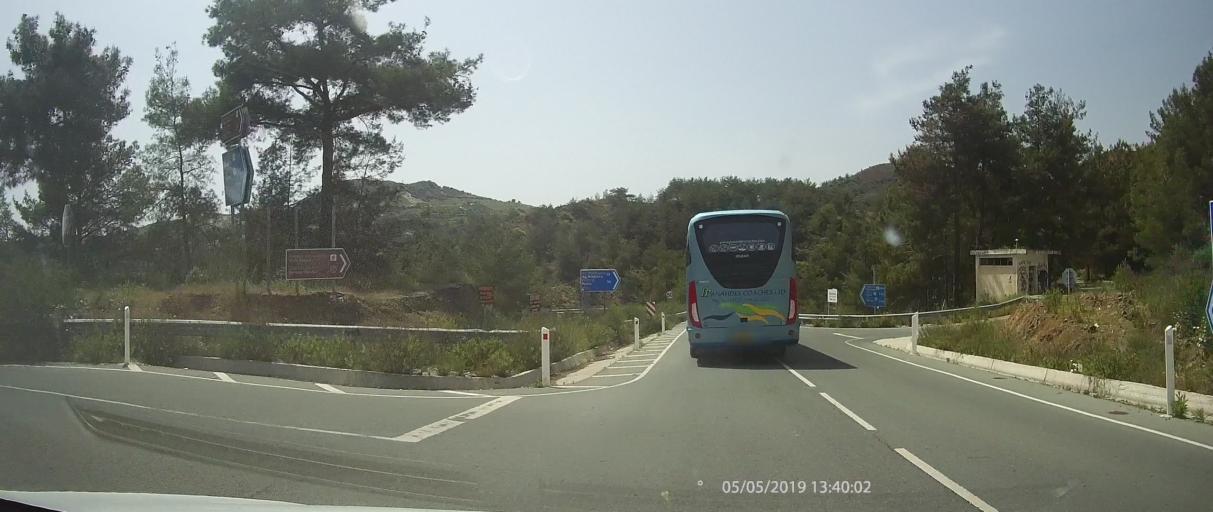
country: CY
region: Limassol
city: Pachna
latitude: 34.8696
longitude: 32.8272
